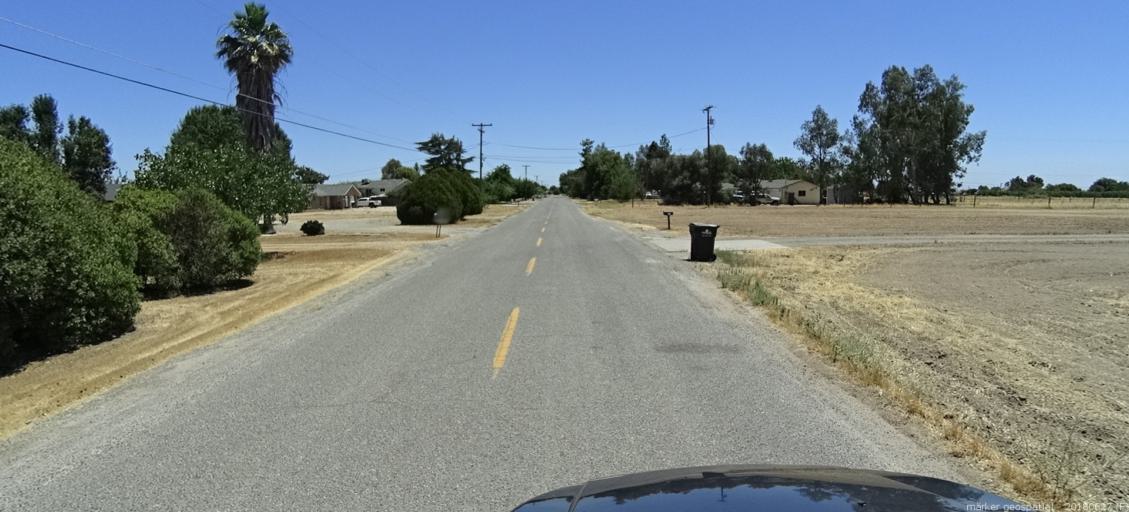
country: US
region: California
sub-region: Madera County
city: Bonadelle Ranchos-Madera Ranchos
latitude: 36.9364
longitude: -119.9165
